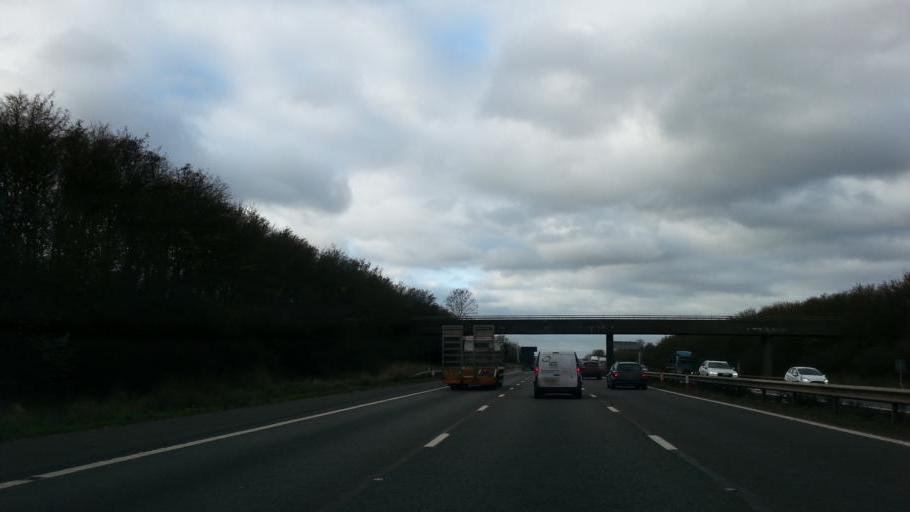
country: GB
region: England
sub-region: Warwickshire
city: Brandon
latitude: 52.4353
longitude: -1.3635
